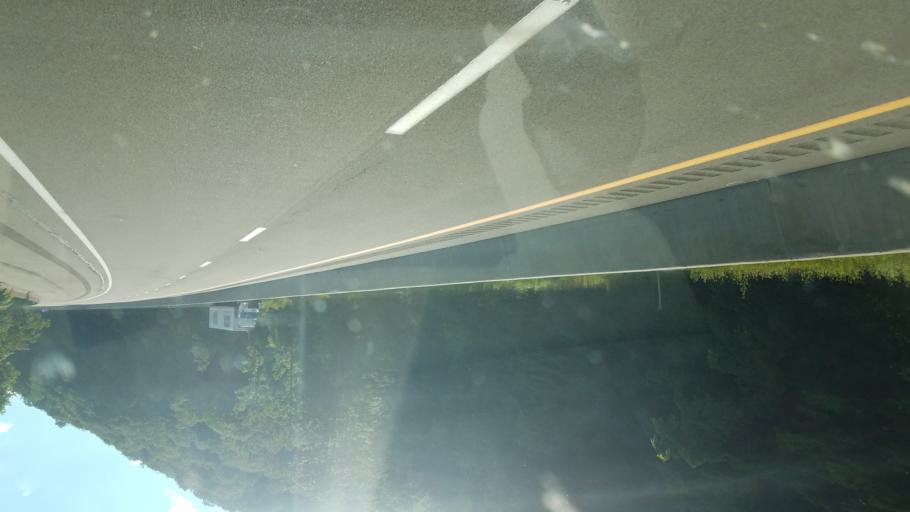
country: US
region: New York
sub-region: Cattaraugus County
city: Salamanca
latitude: 42.1479
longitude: -78.6844
